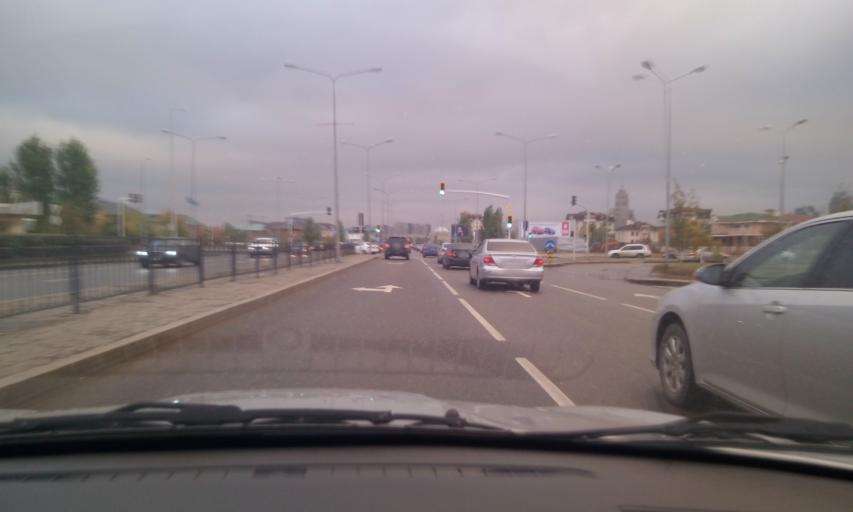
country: KZ
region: Astana Qalasy
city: Astana
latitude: 51.1475
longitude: 71.3956
